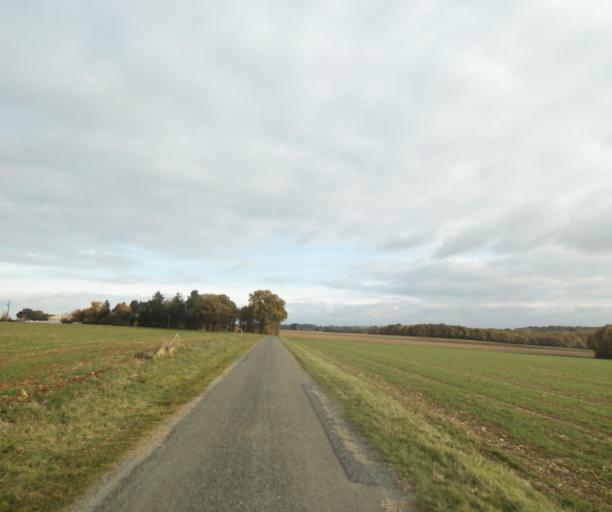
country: FR
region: Poitou-Charentes
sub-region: Departement de la Charente-Maritime
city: Nieul-les-Saintes
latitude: 45.7847
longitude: -0.7359
